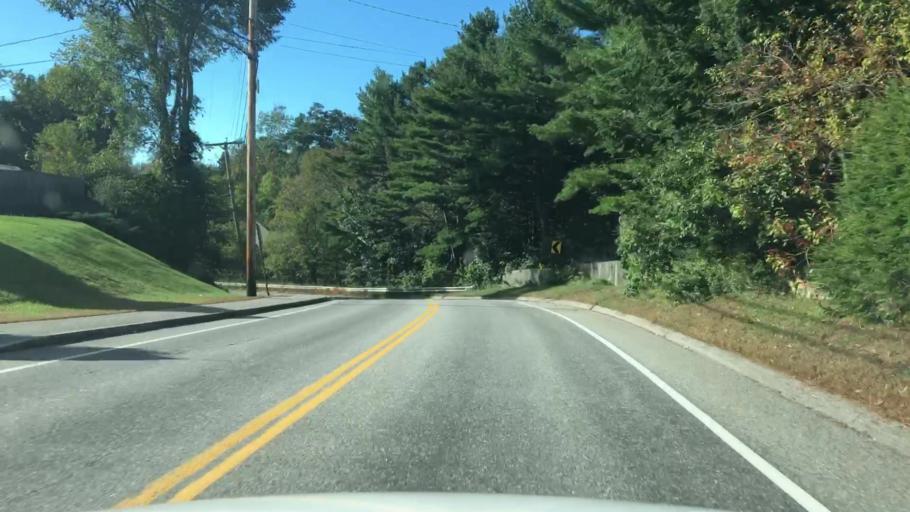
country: US
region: Maine
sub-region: Sagadahoc County
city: Topsham
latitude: 43.9149
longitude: -69.9838
